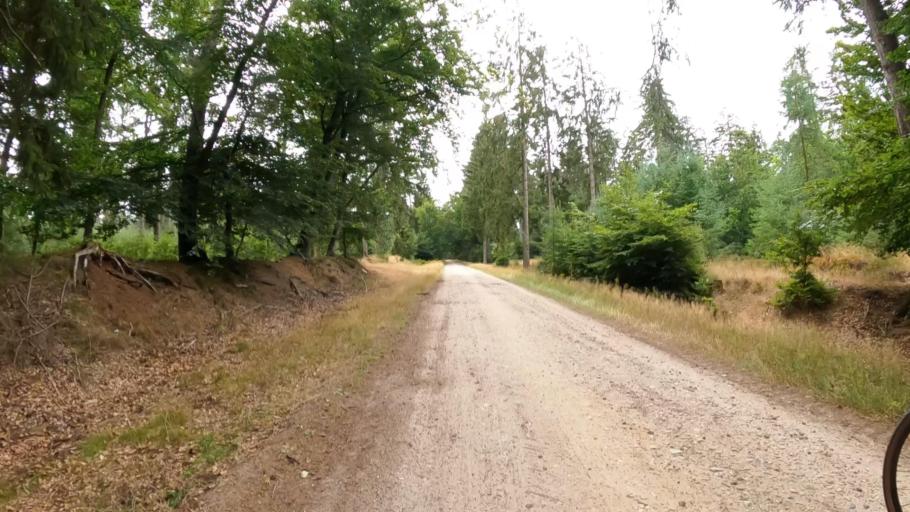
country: DE
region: Schleswig-Holstein
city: Bark
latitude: 53.9430
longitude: 10.1460
